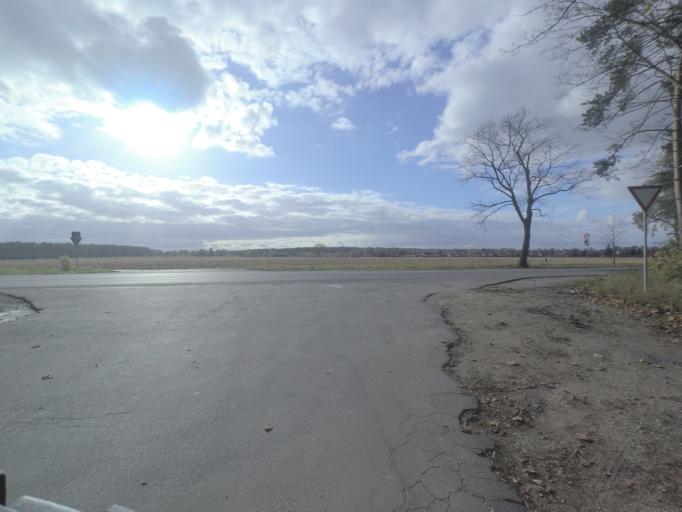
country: DE
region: Brandenburg
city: Ludwigsfelde
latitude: 52.2900
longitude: 13.2776
